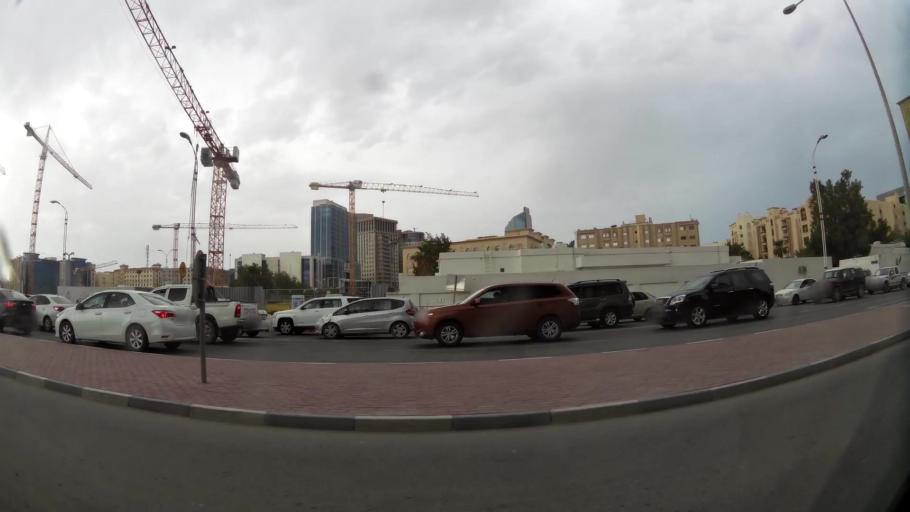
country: QA
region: Baladiyat ad Dawhah
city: Doha
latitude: 25.2818
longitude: 51.5071
